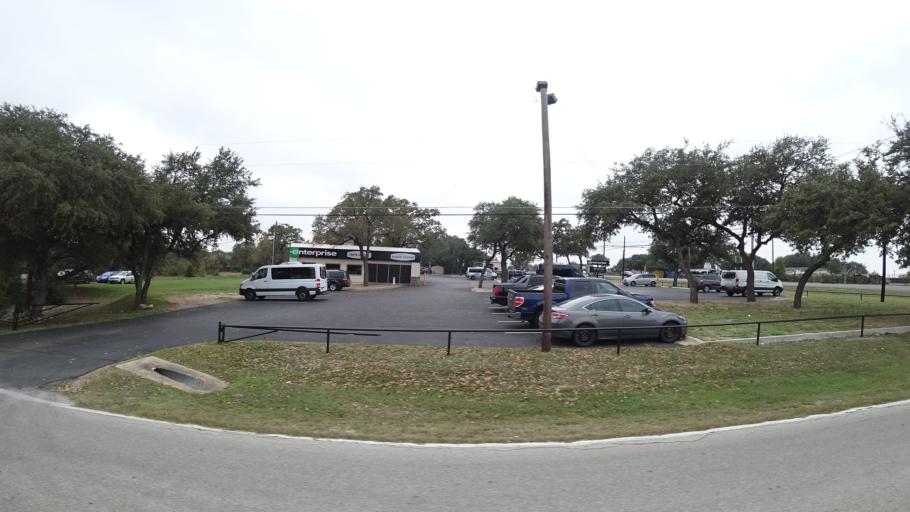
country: US
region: Texas
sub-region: Williamson County
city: Anderson Mill
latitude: 30.4493
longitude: -97.8297
